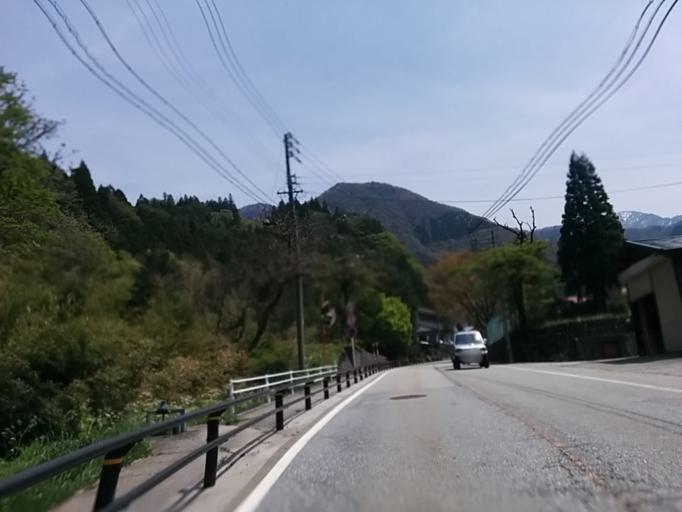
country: JP
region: Gifu
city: Takayama
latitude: 36.2422
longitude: 137.5227
